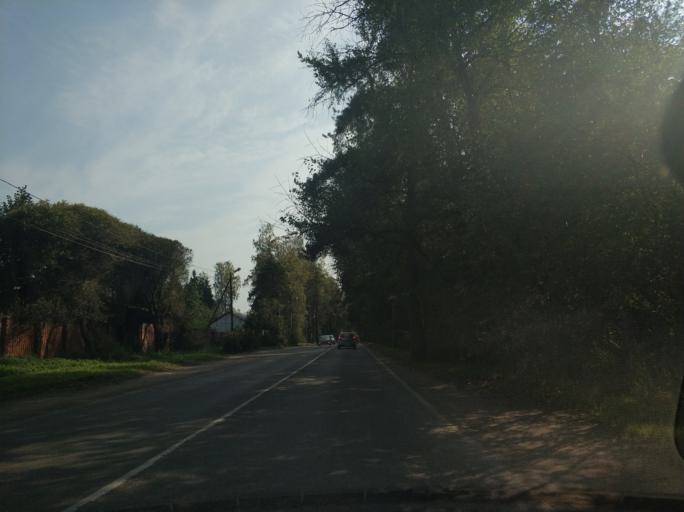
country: RU
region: Leningrad
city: Yanino Vtoroye
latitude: 60.0115
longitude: 30.5939
